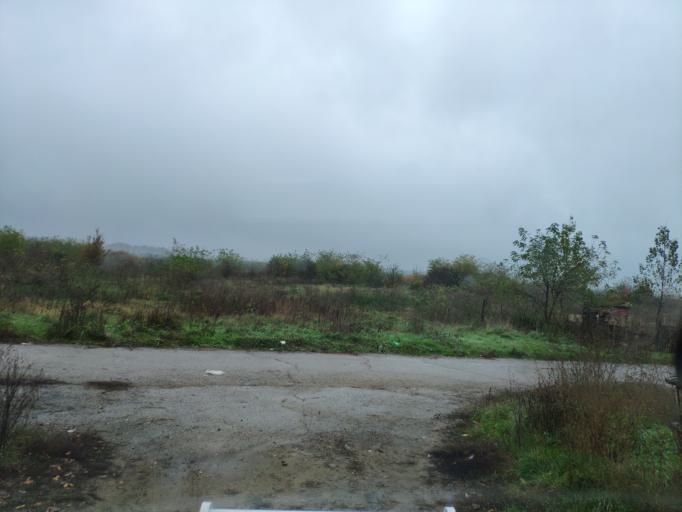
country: SK
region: Kosicky
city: Cierna nad Tisou
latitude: 48.4433
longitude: 21.9996
